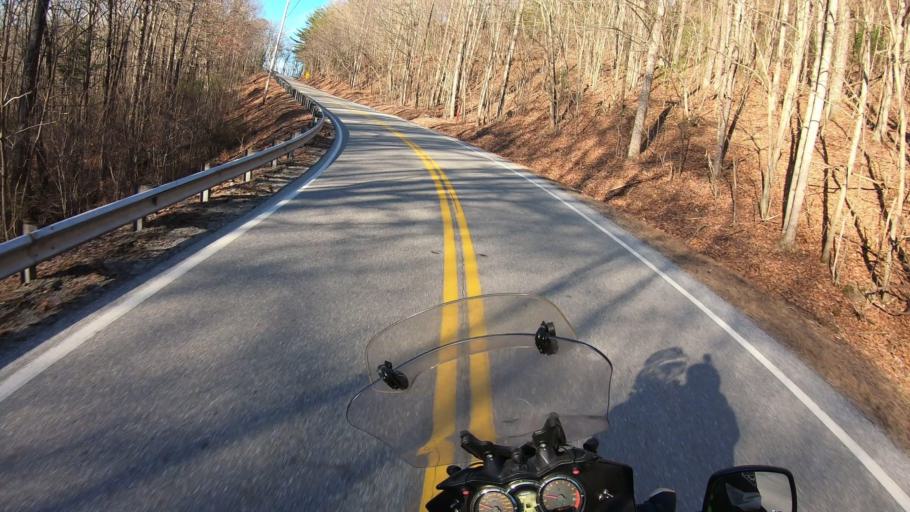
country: US
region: Georgia
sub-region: Lumpkin County
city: Dahlonega
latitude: 34.6869
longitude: -84.0128
